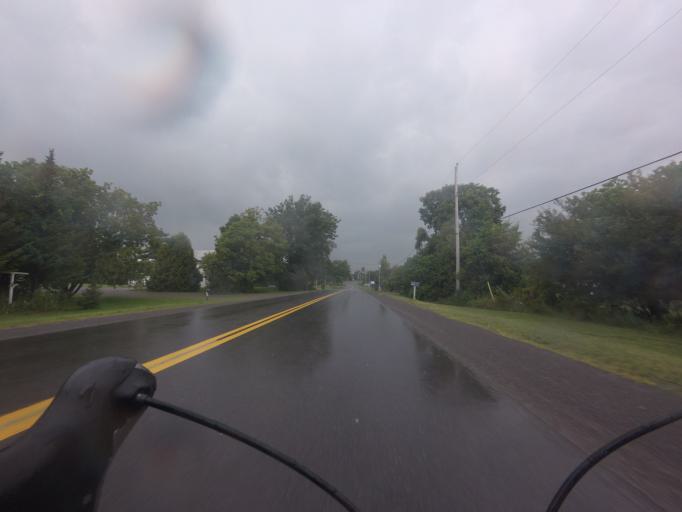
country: CA
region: Ontario
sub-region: Lanark County
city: Smiths Falls
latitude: 44.9064
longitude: -75.8333
